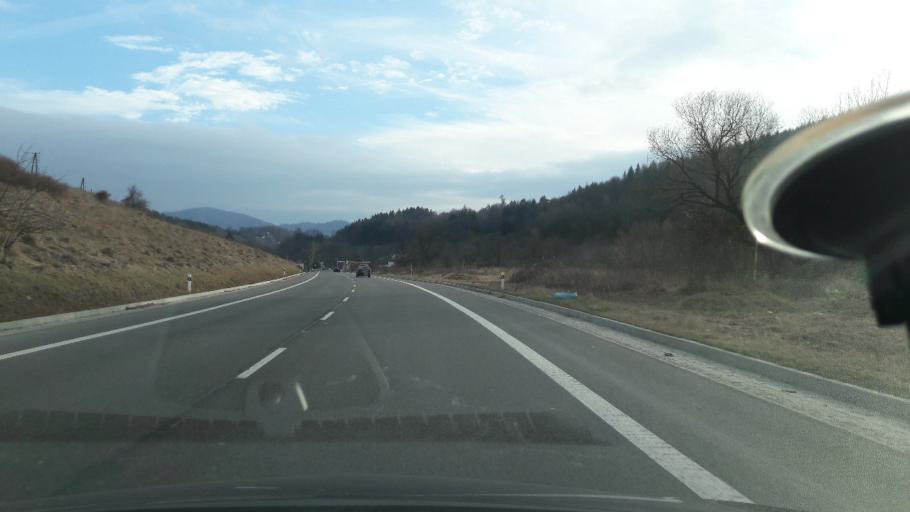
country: SK
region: Nitriansky
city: Handlova
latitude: 48.7530
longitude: 18.7634
